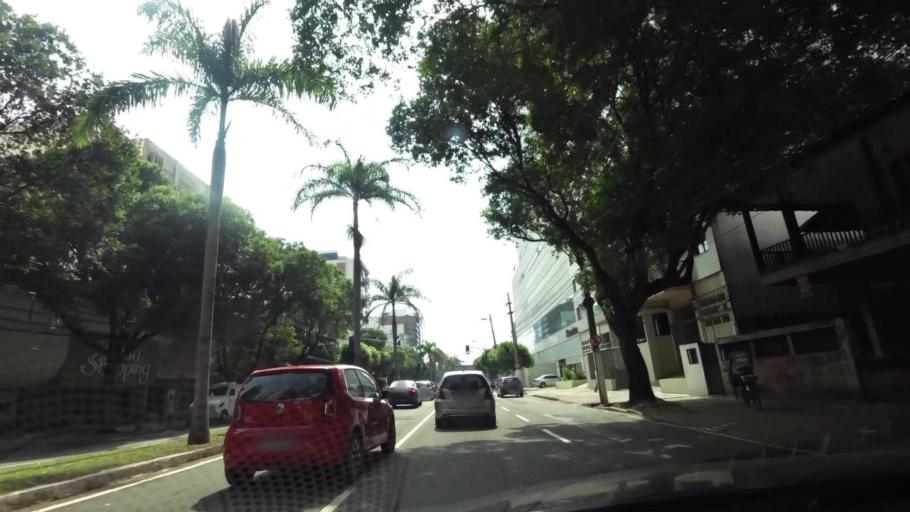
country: BR
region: Espirito Santo
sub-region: Vila Velha
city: Vila Velha
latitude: -20.3061
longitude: -40.2939
